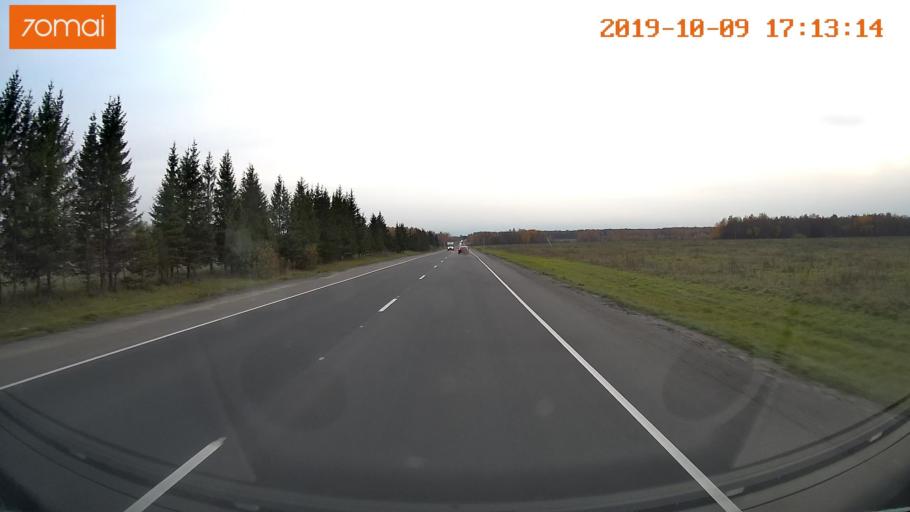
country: RU
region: Ivanovo
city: Privolzhsk
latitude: 57.3177
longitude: 41.2277
